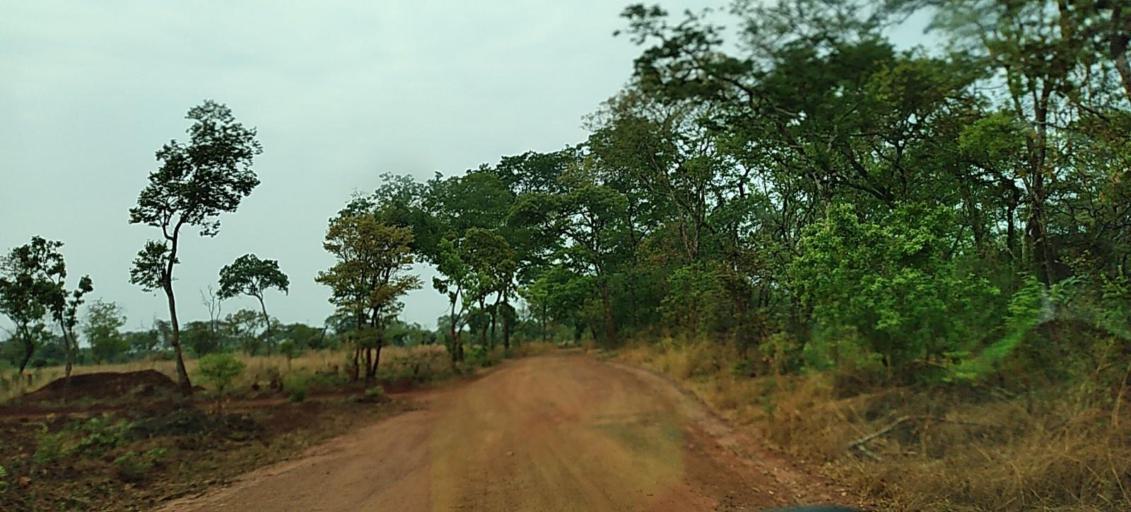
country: ZM
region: North-Western
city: Solwezi
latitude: -12.3171
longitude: 26.5223
